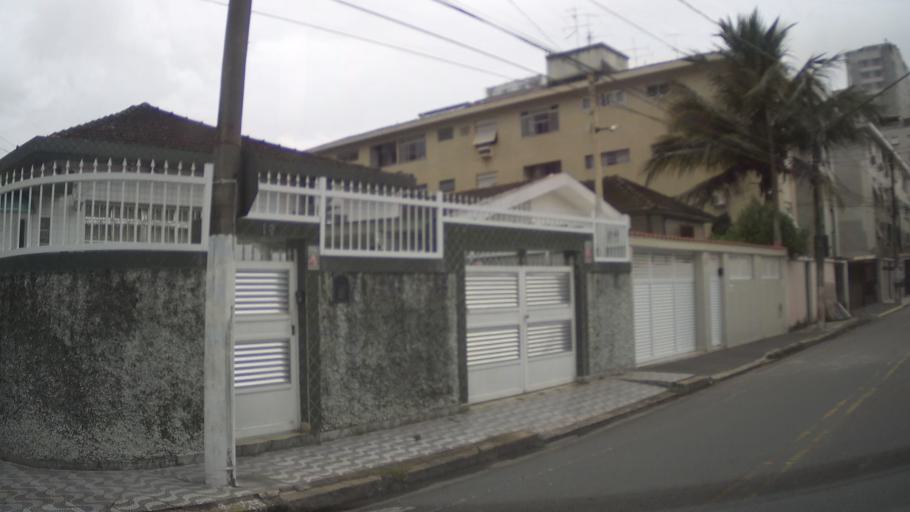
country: BR
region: Sao Paulo
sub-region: Santos
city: Santos
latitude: -23.9719
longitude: -46.3120
